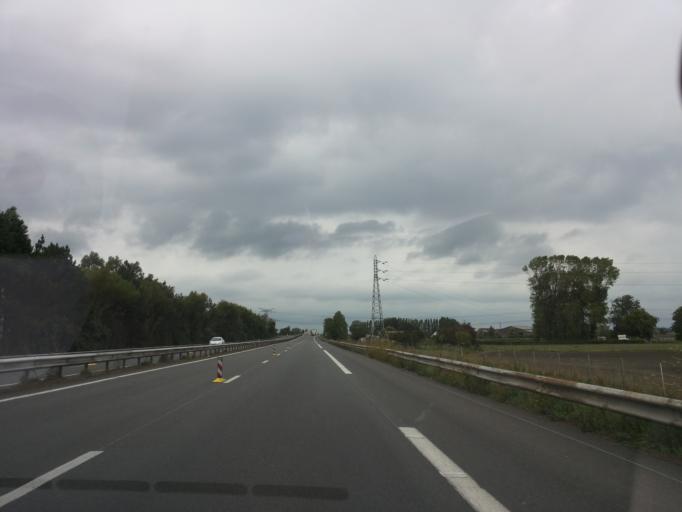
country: FR
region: Nord-Pas-de-Calais
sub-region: Departement du Pas-de-Calais
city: Les Attaques
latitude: 50.9152
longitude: 1.9322
